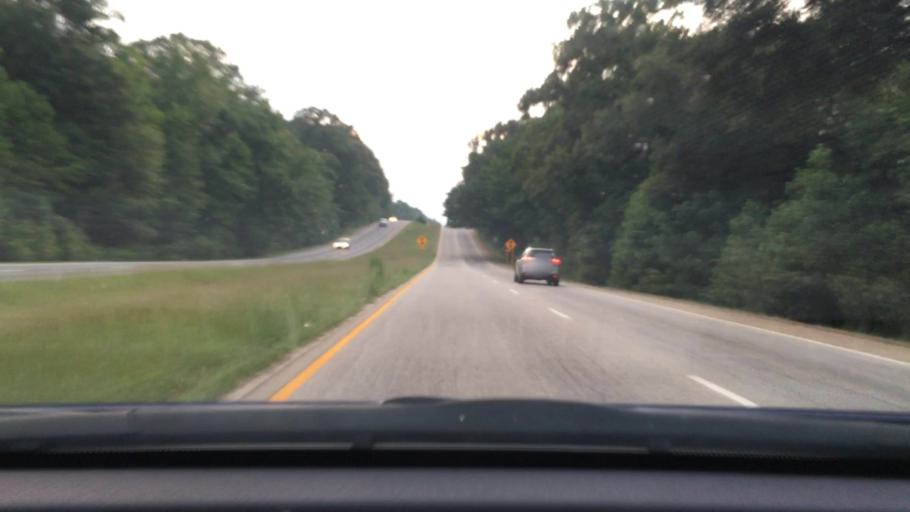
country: US
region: South Carolina
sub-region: Sumter County
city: Stateburg
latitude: 33.9452
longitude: -80.5181
